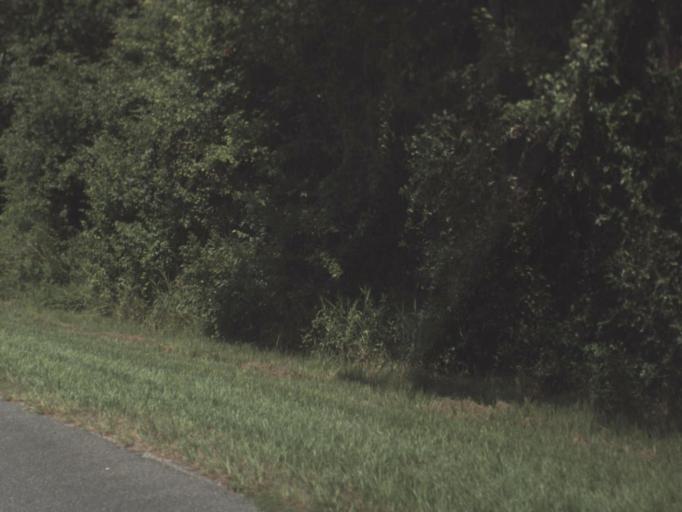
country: US
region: Florida
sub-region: Union County
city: Lake Butler
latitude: 30.0293
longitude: -82.3189
